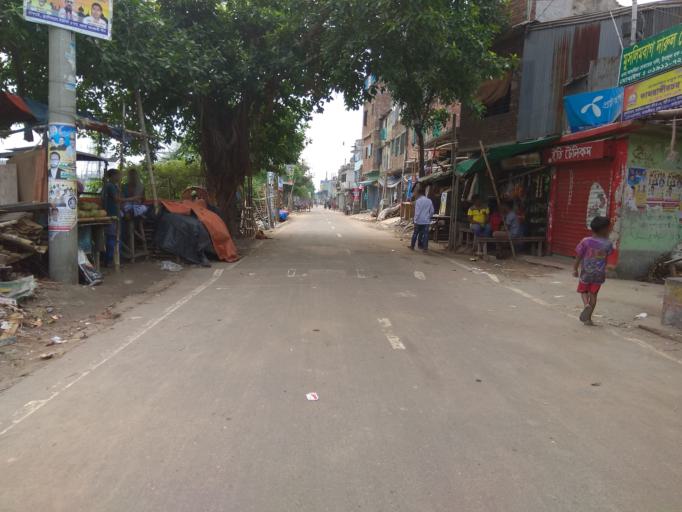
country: BD
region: Dhaka
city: Azimpur
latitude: 23.7110
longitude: 90.3865
